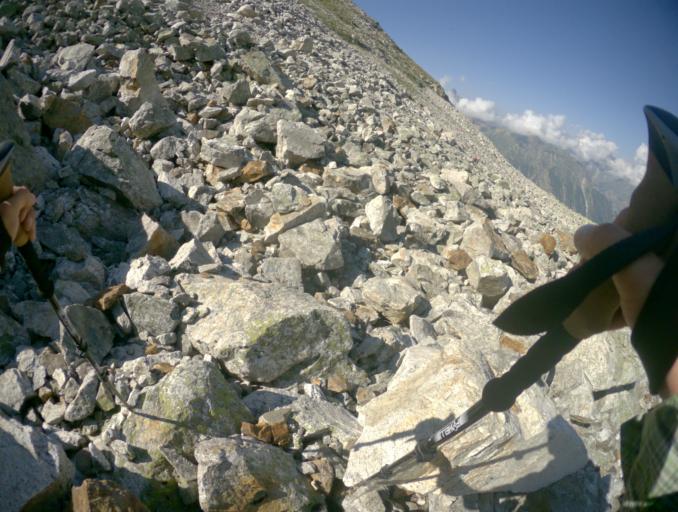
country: RU
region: Karachayevo-Cherkesiya
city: Uchkulan
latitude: 43.3072
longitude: 42.0656
